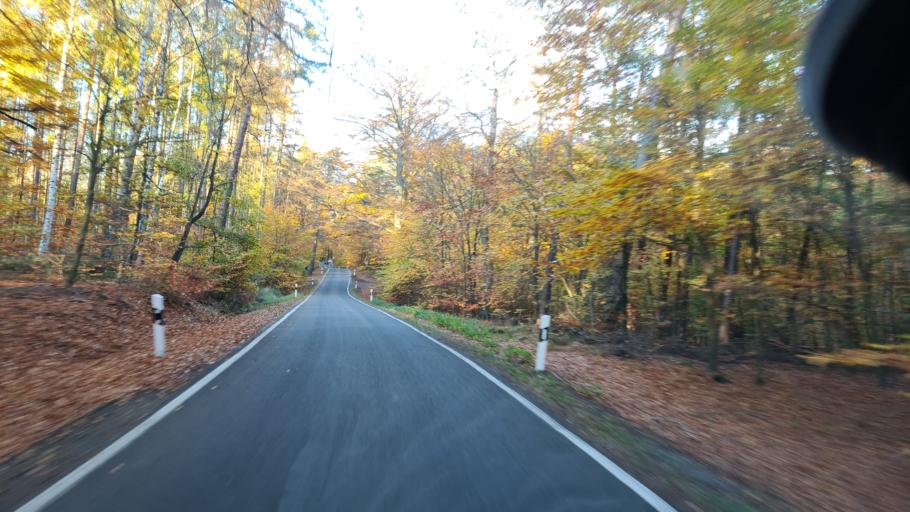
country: DE
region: Saxony
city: Dahlen
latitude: 51.4202
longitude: 13.0377
